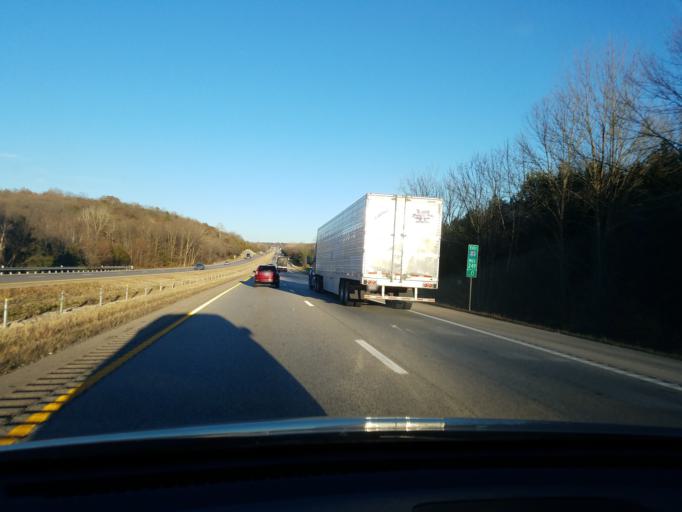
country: US
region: Missouri
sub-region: Franklin County
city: Villa Ridge
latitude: 38.4518
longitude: -90.8887
